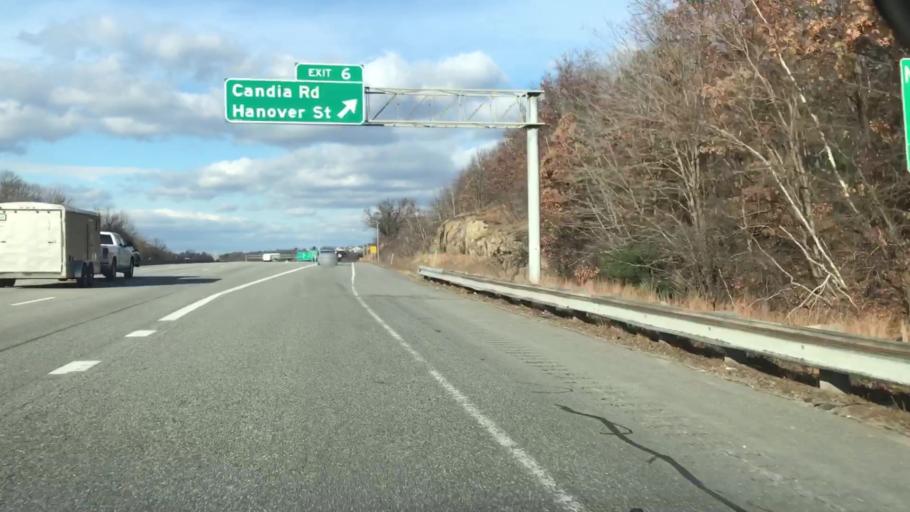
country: US
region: New Hampshire
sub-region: Hillsborough County
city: Manchester
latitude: 42.9786
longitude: -71.4143
